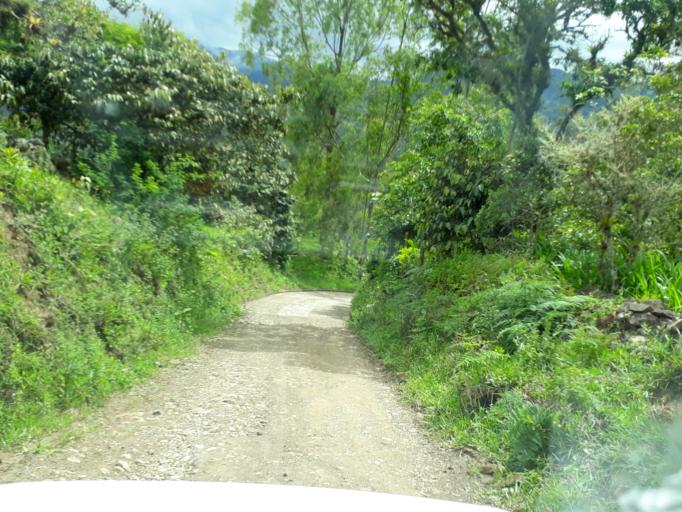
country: CO
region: Cundinamarca
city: Gacheta
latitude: 4.8120
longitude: -73.6430
